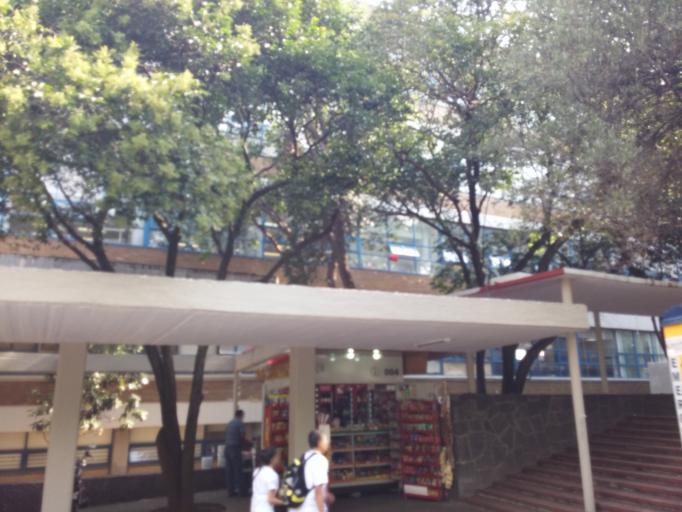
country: MX
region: Mexico City
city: Coyoacan
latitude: 19.3349
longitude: -99.1811
